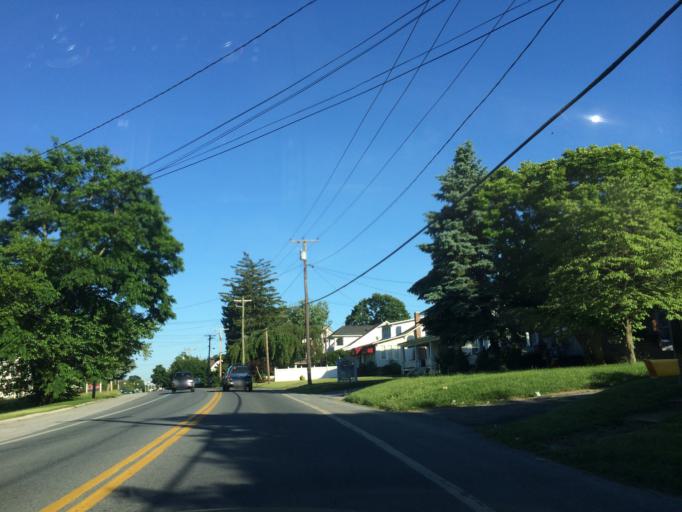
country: US
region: Maryland
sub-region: Carroll County
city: Westminster
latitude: 39.5639
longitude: -76.9840
